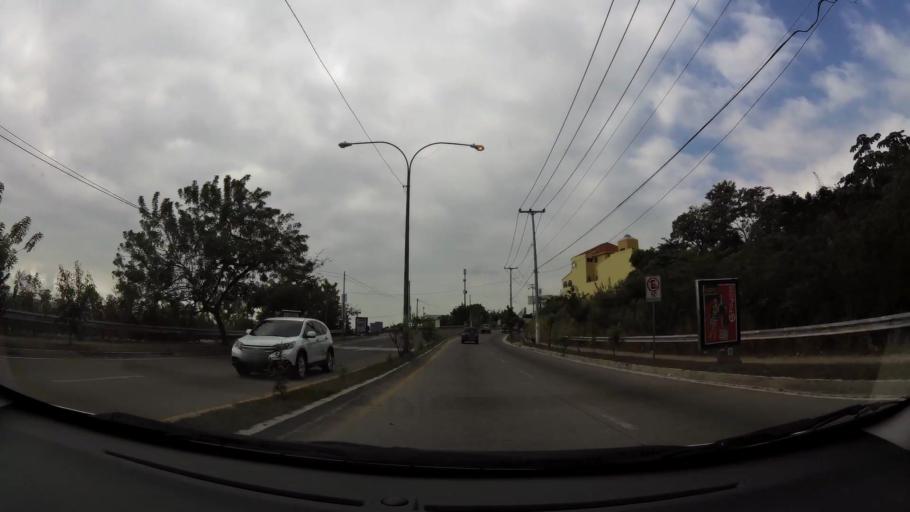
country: SV
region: San Salvador
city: Mejicanos
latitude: 13.7189
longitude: -89.2423
